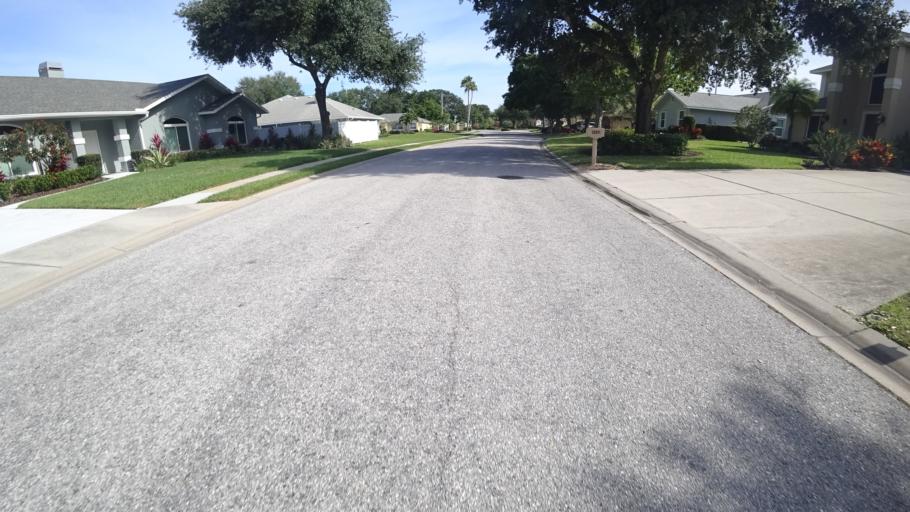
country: US
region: Florida
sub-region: Manatee County
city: West Bradenton
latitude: 27.5134
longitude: -82.6533
